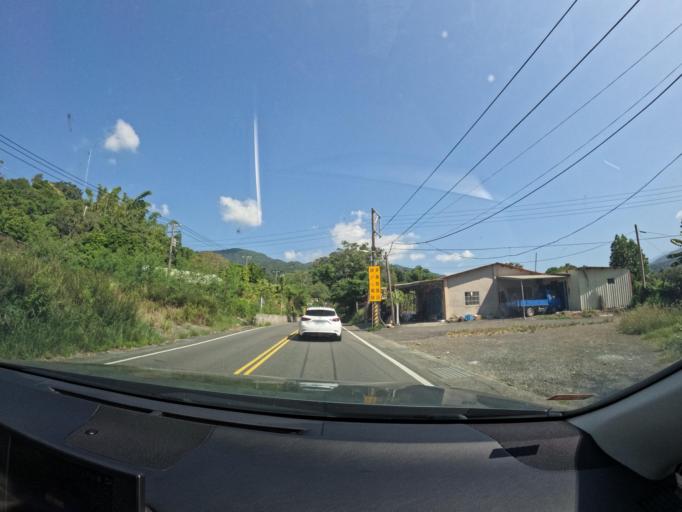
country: TW
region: Taiwan
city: Yujing
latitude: 23.0845
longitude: 120.6794
